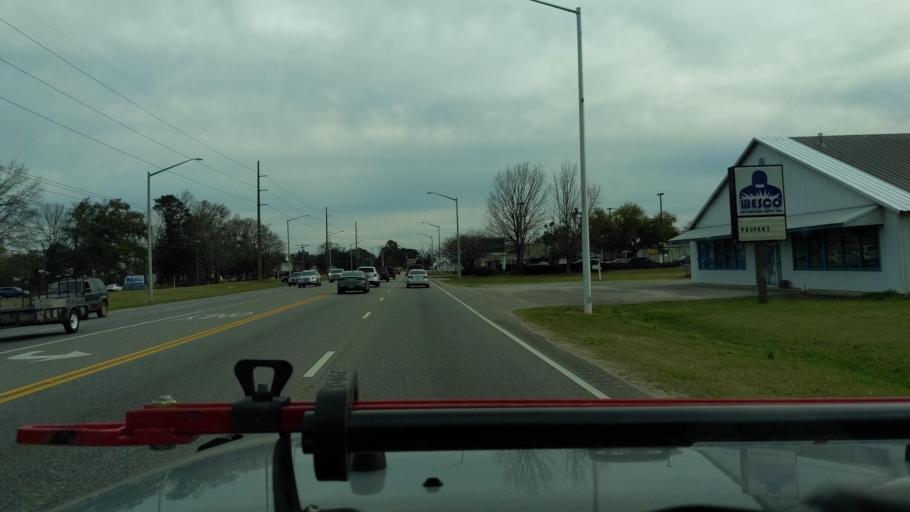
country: US
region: Alabama
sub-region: Baldwin County
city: Foley
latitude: 30.4211
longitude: -87.6833
